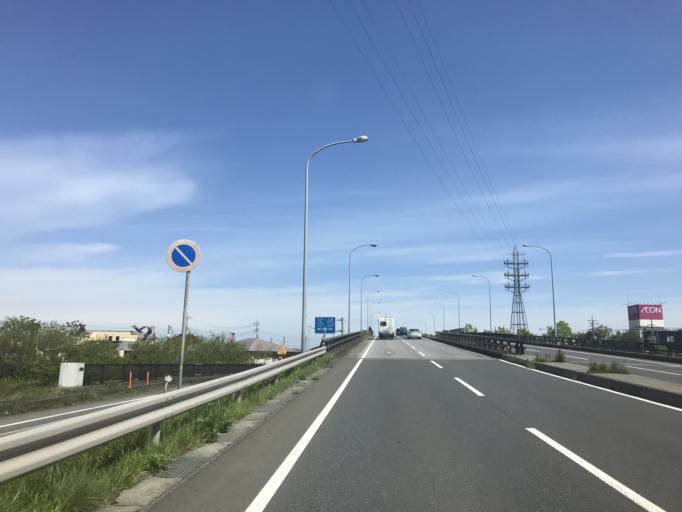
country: JP
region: Ibaraki
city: Ishige
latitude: 36.1865
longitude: 139.9887
